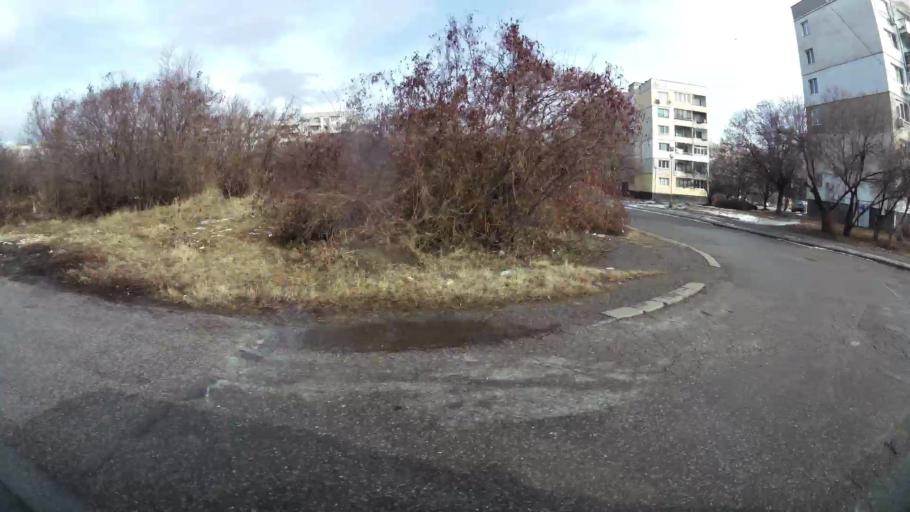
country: BG
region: Sofia-Capital
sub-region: Stolichna Obshtina
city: Sofia
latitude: 42.7157
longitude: 23.2731
